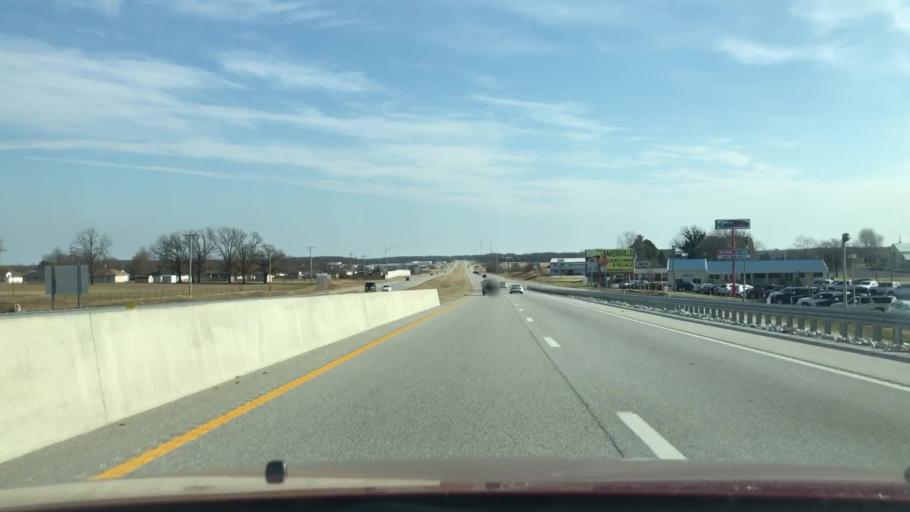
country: US
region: Missouri
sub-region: Webster County
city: Rogersville
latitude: 37.1109
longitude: -93.0550
